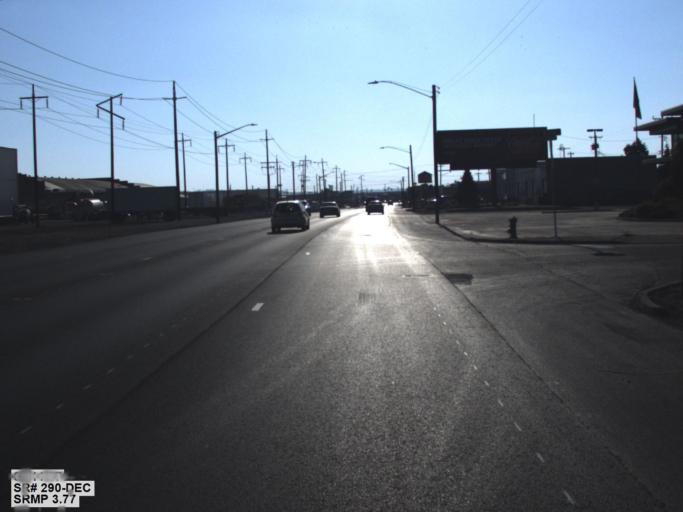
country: US
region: Washington
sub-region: Spokane County
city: Millwood
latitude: 47.6737
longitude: -117.3360
